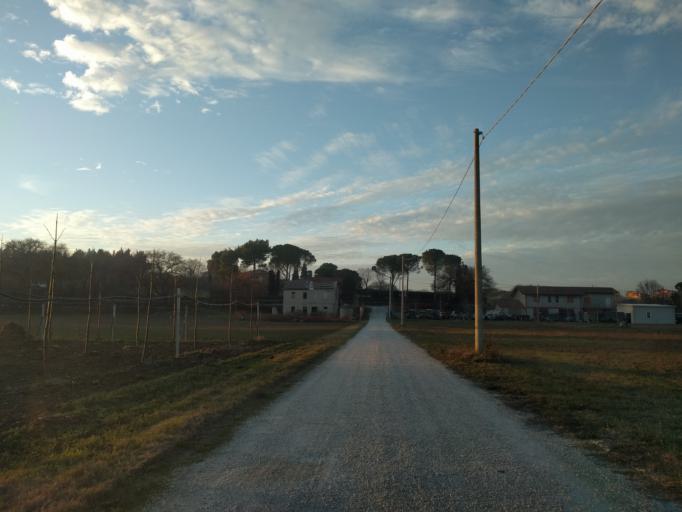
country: IT
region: The Marches
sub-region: Provincia di Pesaro e Urbino
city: Lucrezia
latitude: 43.7665
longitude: 12.9324
